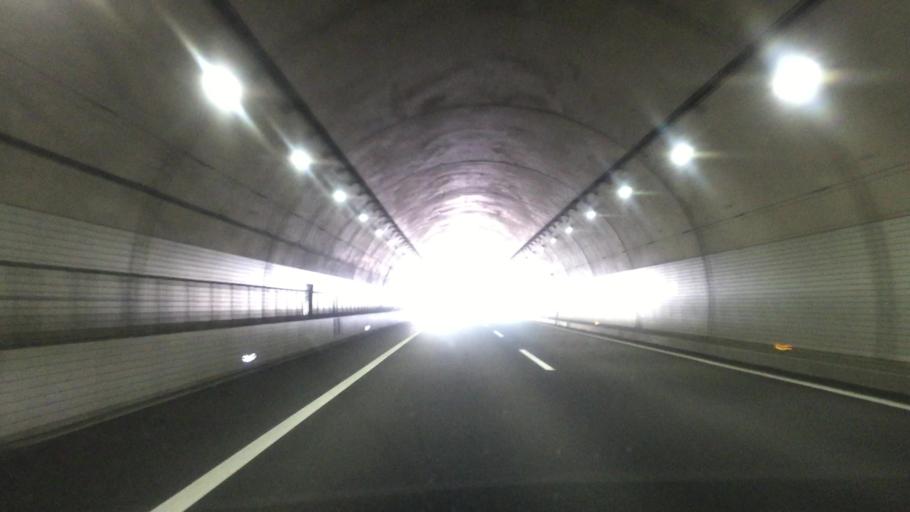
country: JP
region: Aichi
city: Okazaki
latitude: 34.9418
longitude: 137.2586
